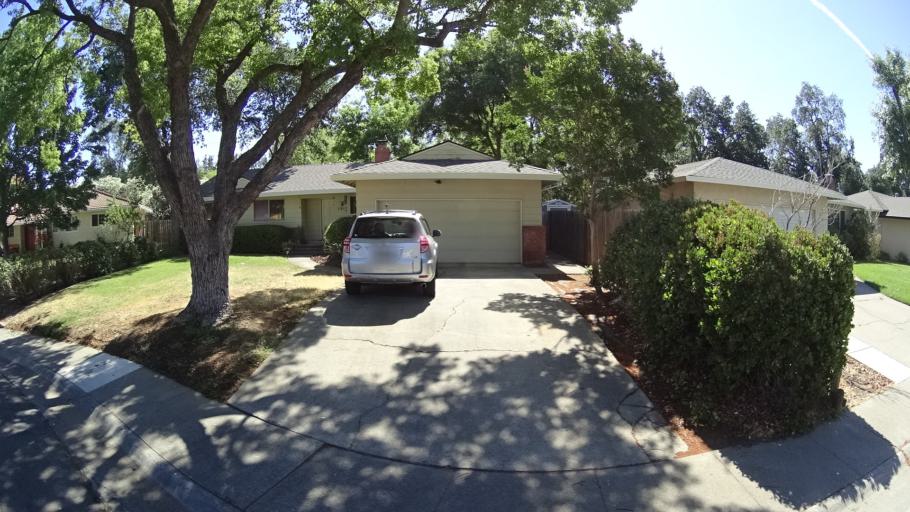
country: US
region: California
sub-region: Sacramento County
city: Parkway
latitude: 38.5001
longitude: -121.5070
